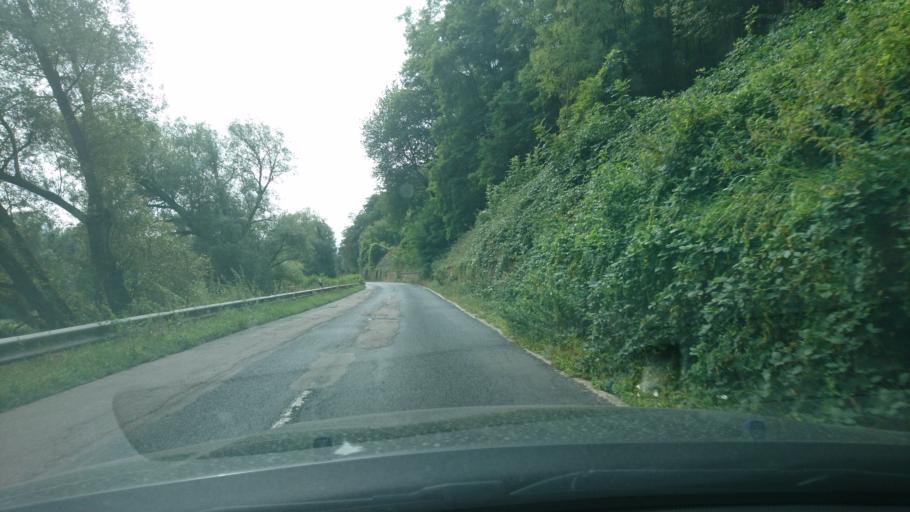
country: DE
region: Rheinland-Pfalz
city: Wiltingen
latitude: 49.6634
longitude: 6.5859
